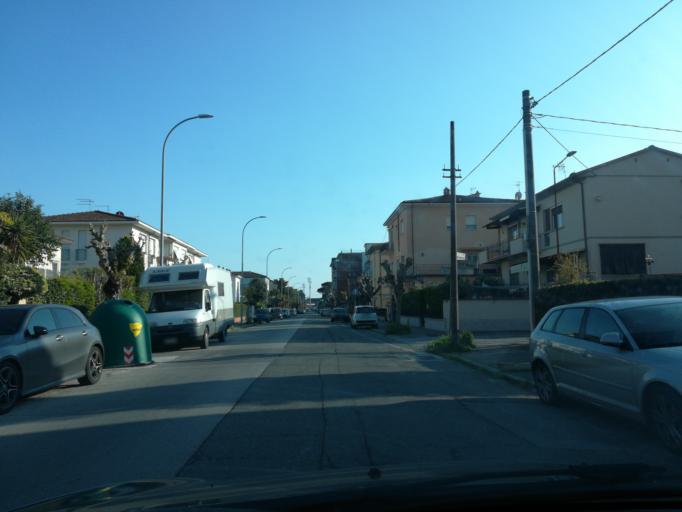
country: IT
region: Tuscany
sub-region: Province of Pisa
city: Pisa
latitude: 43.7323
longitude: 10.4004
